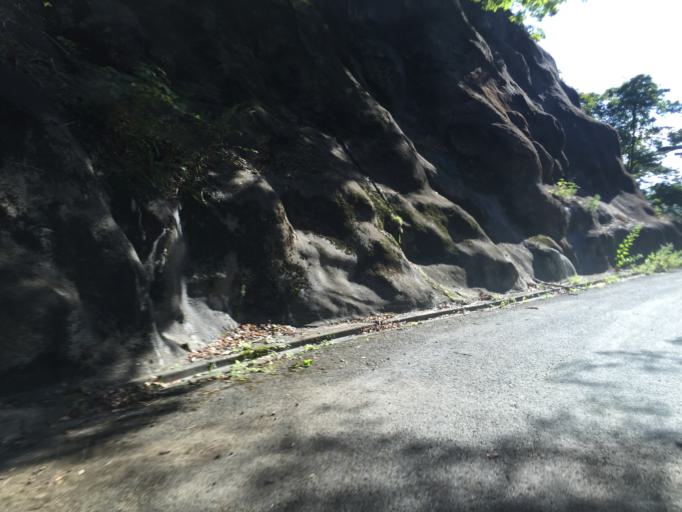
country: JP
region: Fukushima
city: Yanagawamachi-saiwaicho
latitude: 37.8471
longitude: 140.6840
